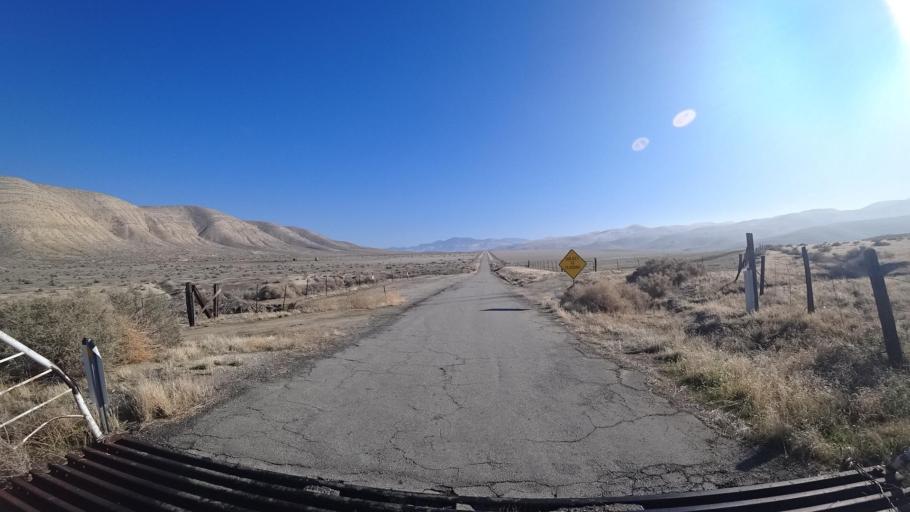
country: US
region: California
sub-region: Kern County
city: Maricopa
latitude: 35.0048
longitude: -119.4086
